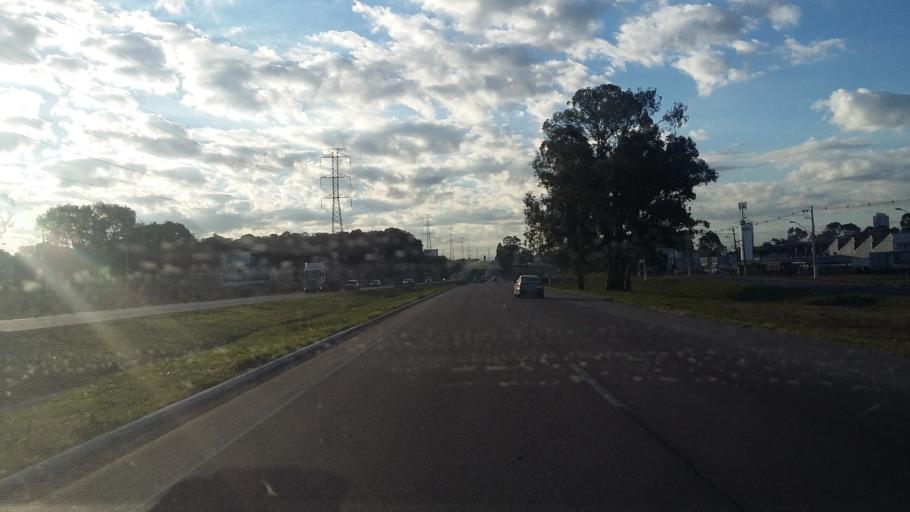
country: BR
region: Parana
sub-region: Curitiba
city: Curitiba
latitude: -25.4658
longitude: -49.3566
